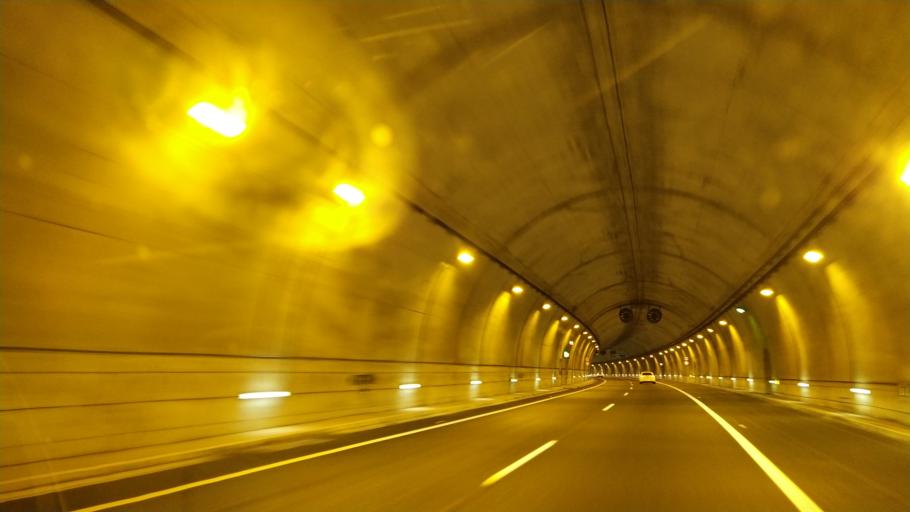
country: ES
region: Cantabria
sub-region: Provincia de Cantabria
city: Camargo
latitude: 43.3939
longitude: -3.8667
